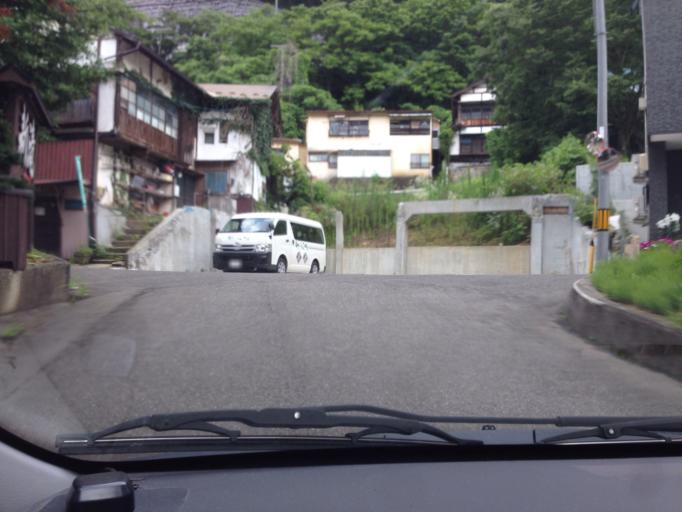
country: JP
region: Fukushima
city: Inawashiro
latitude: 37.4777
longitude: 139.9633
